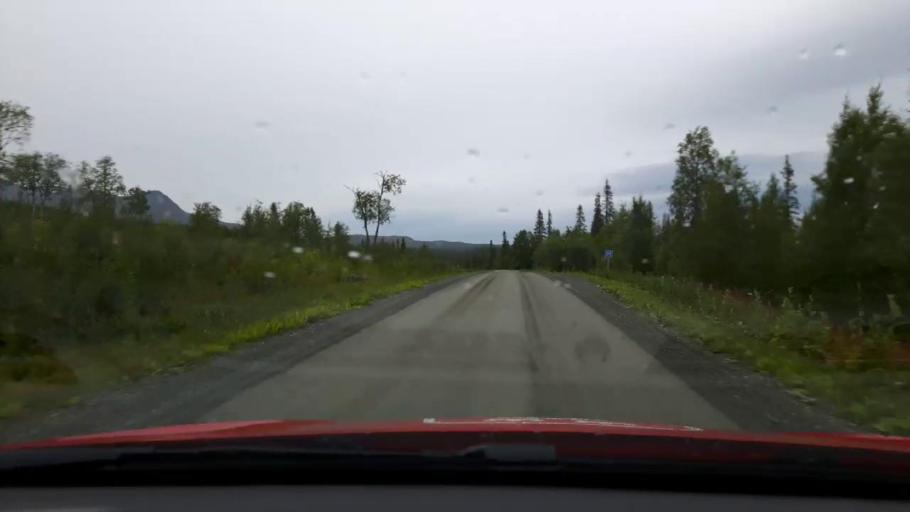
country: SE
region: Jaemtland
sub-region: Are Kommun
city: Are
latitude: 63.4175
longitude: 13.2264
